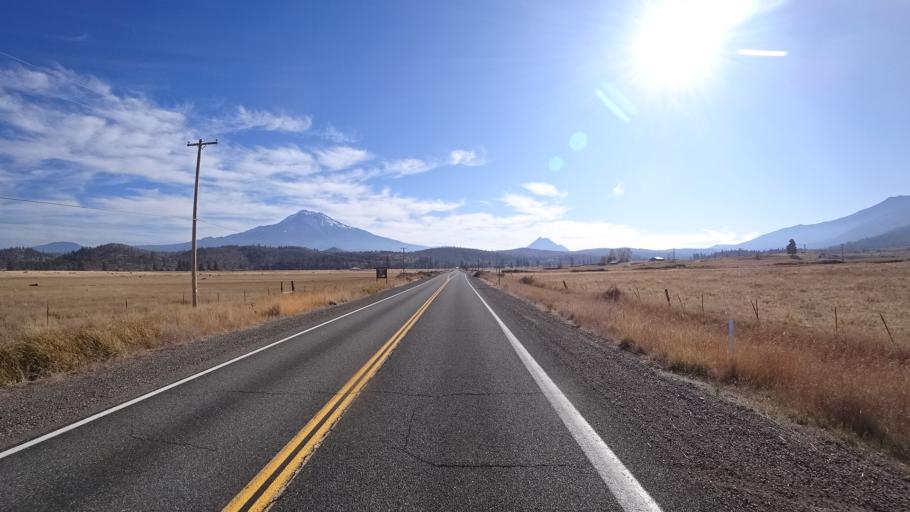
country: US
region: California
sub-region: Siskiyou County
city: Weed
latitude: 41.4452
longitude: -122.4444
